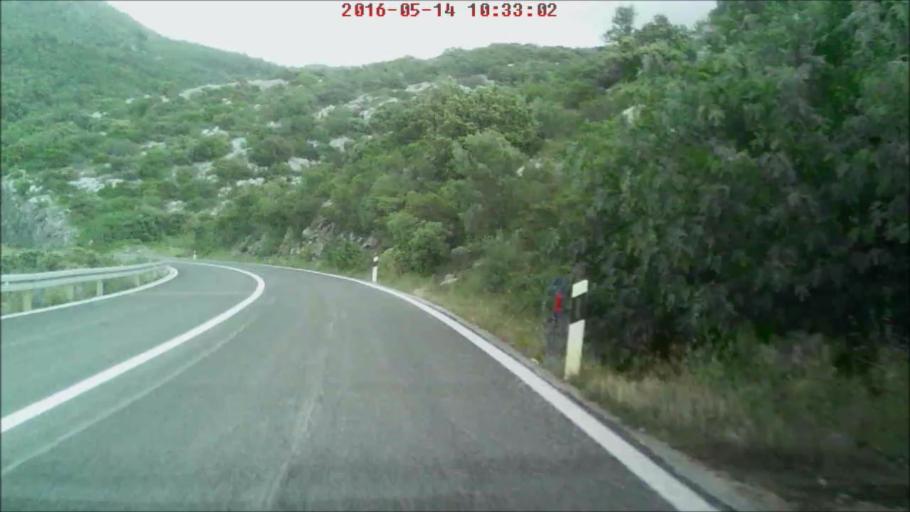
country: HR
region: Dubrovacko-Neretvanska
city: Podgora
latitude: 42.7718
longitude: 17.8828
